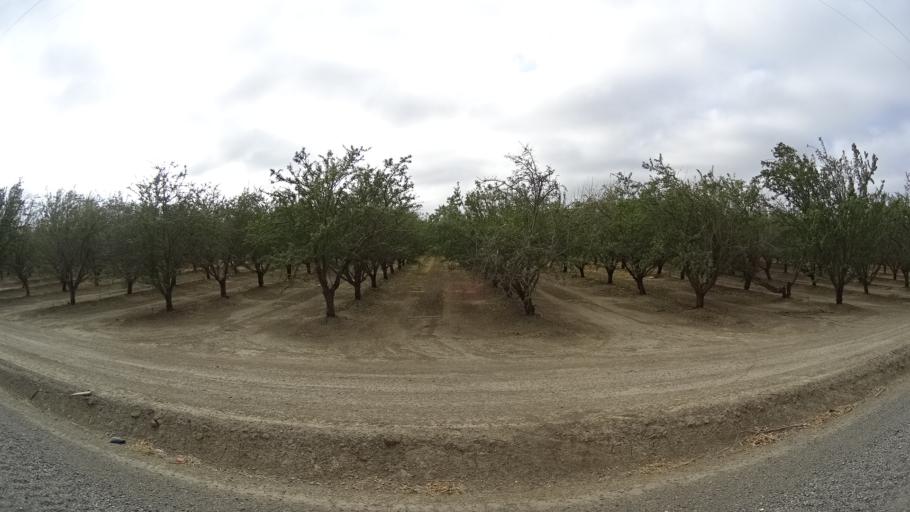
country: US
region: California
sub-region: Yolo County
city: Woodland
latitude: 38.7935
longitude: -121.8119
